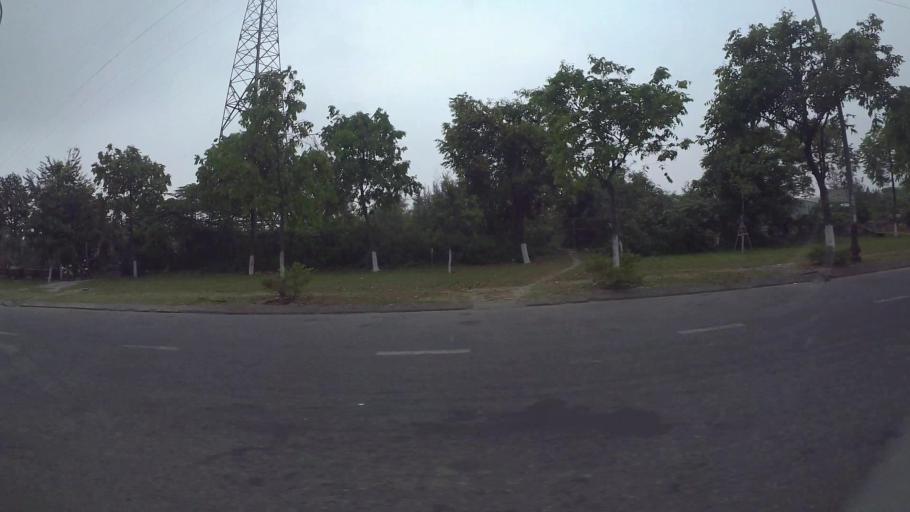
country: VN
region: Da Nang
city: Cam Le
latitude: 16.0268
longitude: 108.2204
